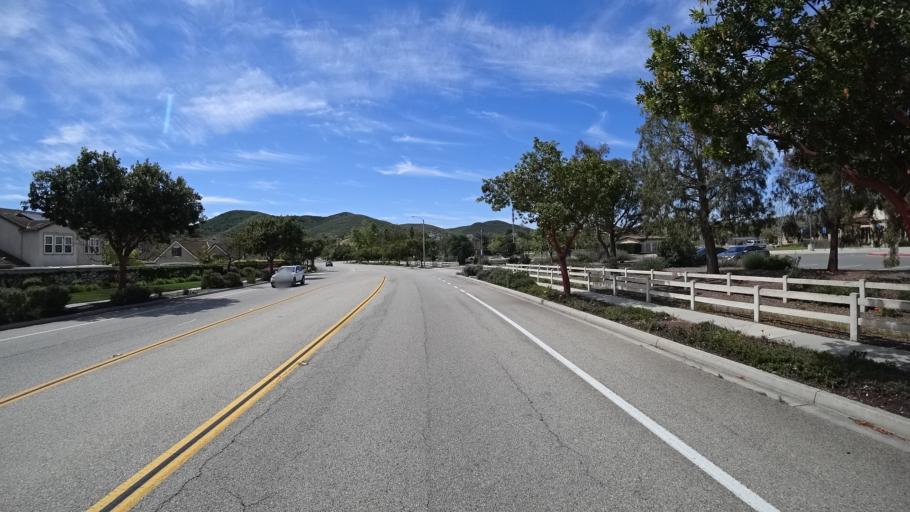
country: US
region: California
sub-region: Ventura County
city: Casa Conejo
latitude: 34.1757
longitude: -118.9815
